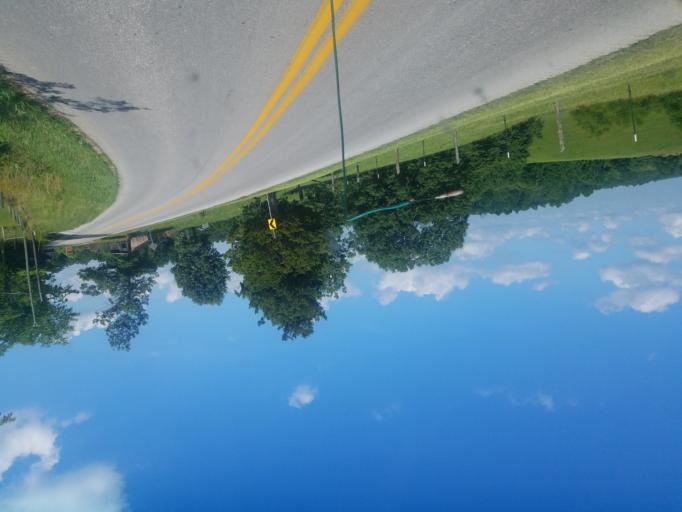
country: US
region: Kentucky
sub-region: Hart County
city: Munfordville
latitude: 37.3088
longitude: -85.9473
